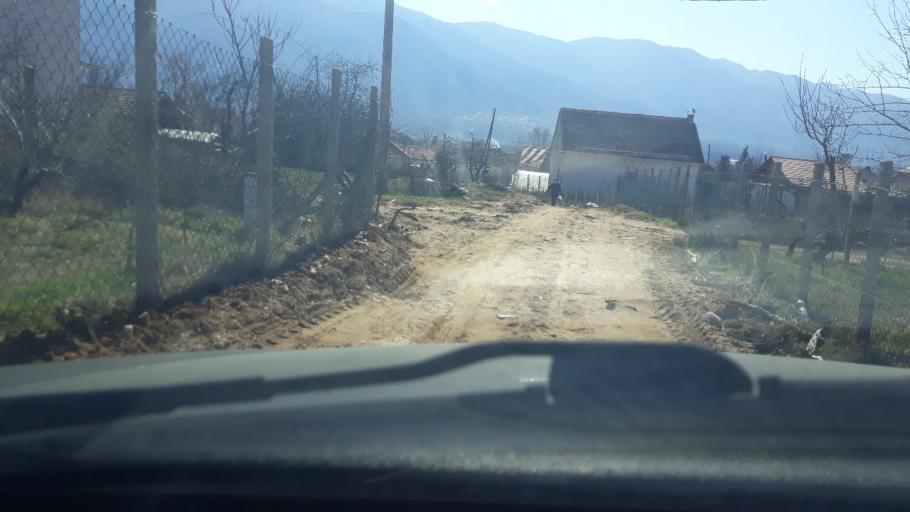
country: MK
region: Novo Selo
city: Novo Selo
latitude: 41.4172
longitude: 22.8803
